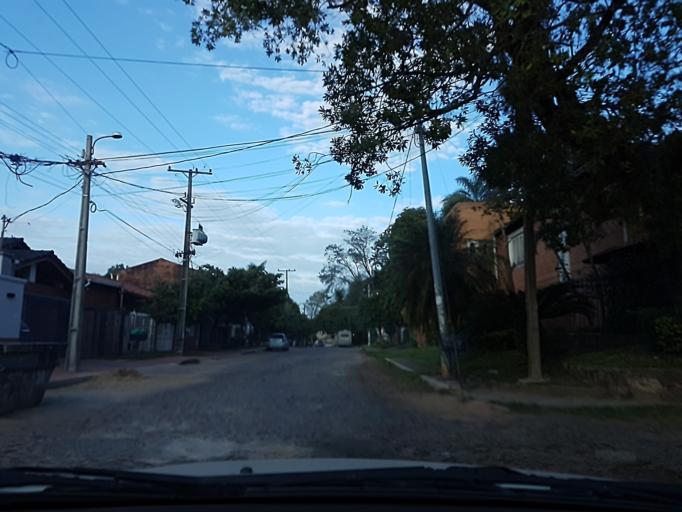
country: PY
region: Central
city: Fernando de la Mora
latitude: -25.2731
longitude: -57.5529
